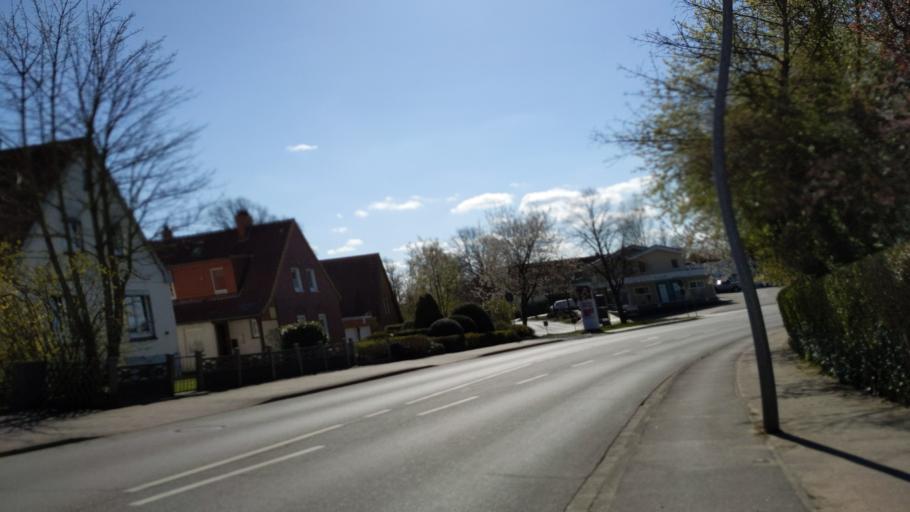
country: DE
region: Schleswig-Holstein
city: Eutin
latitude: 54.1293
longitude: 10.5838
